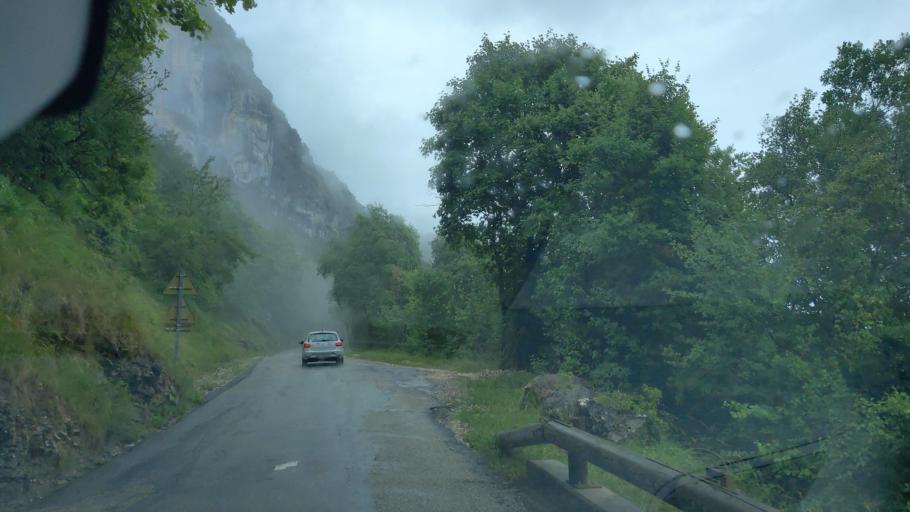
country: FR
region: Rhone-Alpes
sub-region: Departement de la Savoie
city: Chatillon
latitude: 45.7842
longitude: 5.8672
